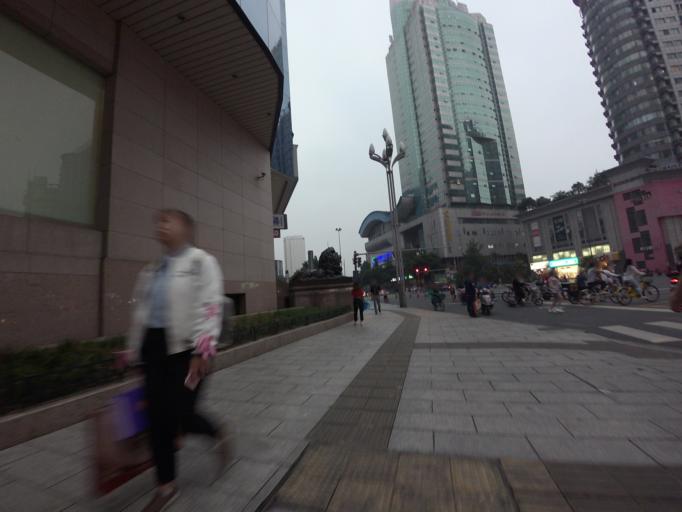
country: CN
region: Sichuan
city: Chengdu
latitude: 30.6721
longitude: 104.0637
